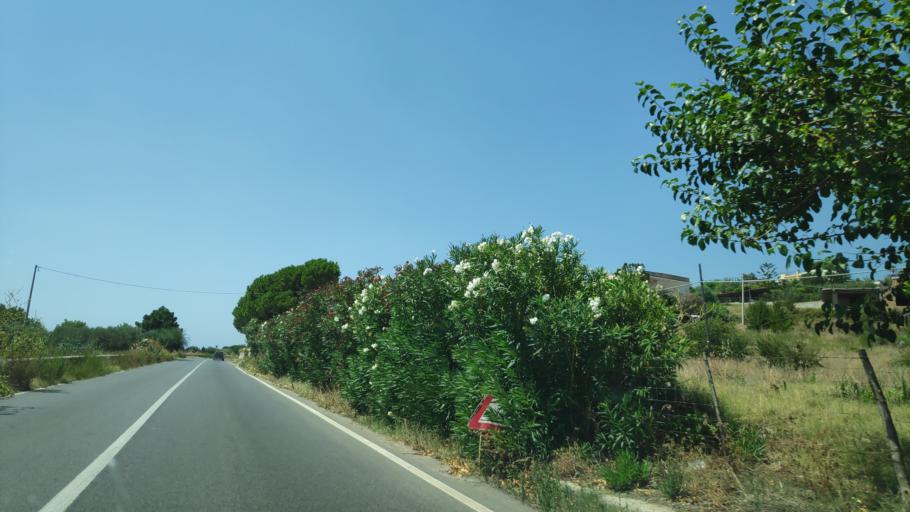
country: IT
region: Calabria
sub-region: Provincia di Reggio Calabria
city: Weather Station
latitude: 37.9400
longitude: 16.0782
